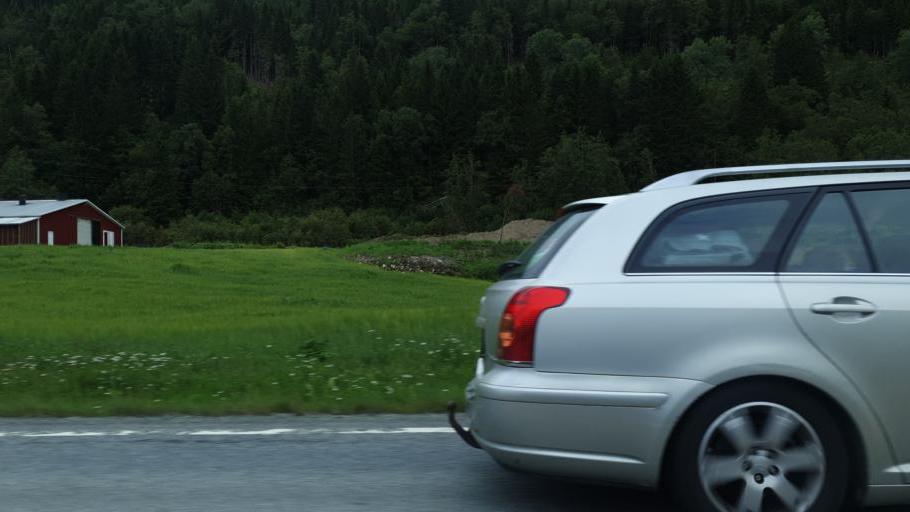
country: NO
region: Sor-Trondelag
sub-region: Midtre Gauldal
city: Storen
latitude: 63.0077
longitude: 10.2412
